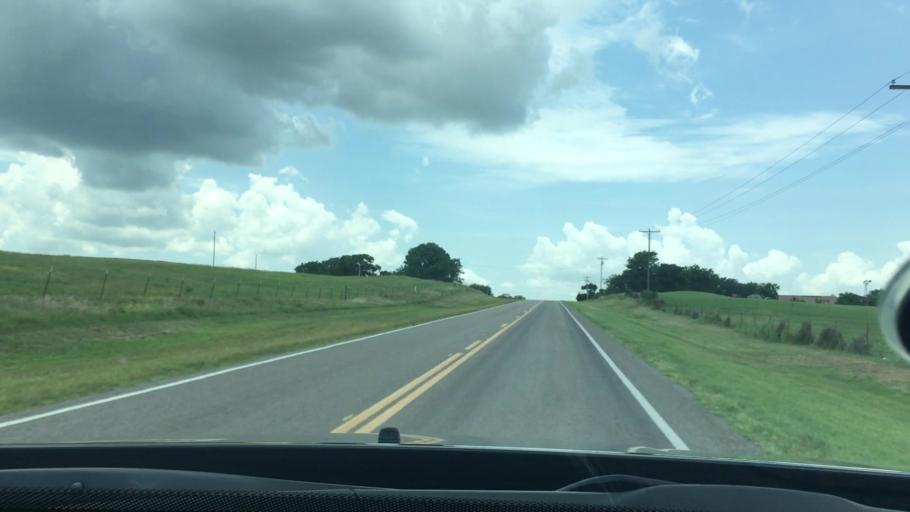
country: US
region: Oklahoma
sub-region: Carter County
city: Wilson
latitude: 33.9403
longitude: -97.3721
